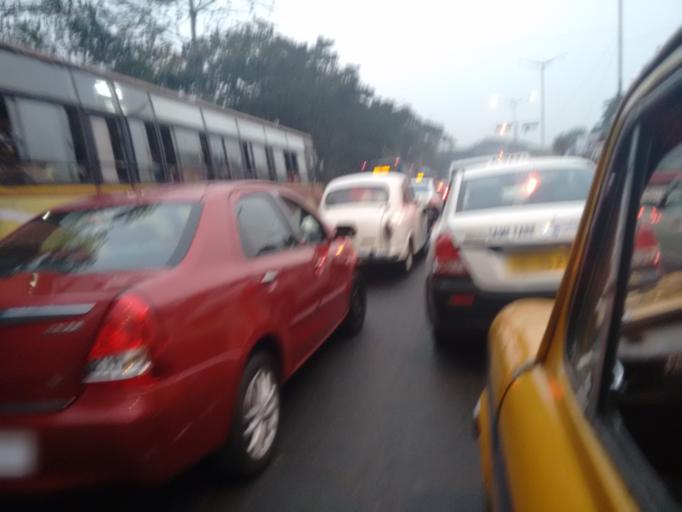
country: IN
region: West Bengal
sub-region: Kolkata
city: Kolkata
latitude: 22.5701
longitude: 88.4044
